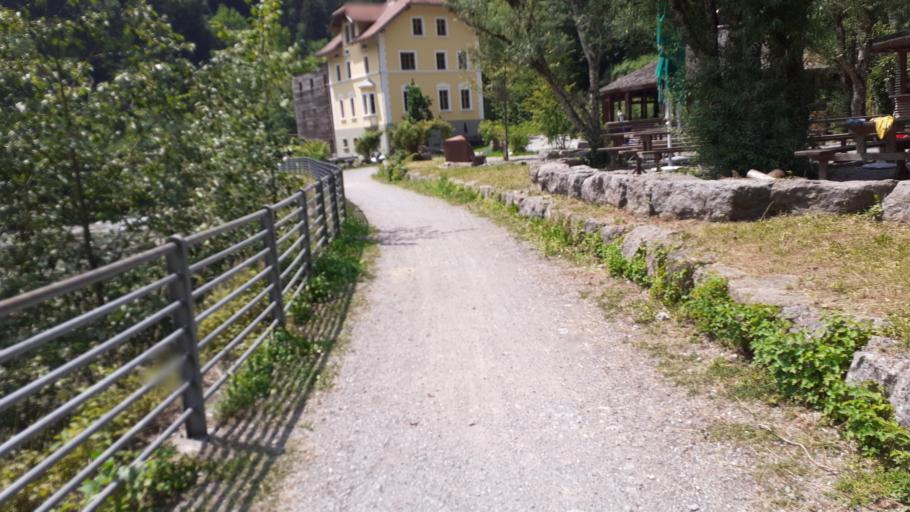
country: AT
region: Vorarlberg
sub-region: Politischer Bezirk Bregenz
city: Egg
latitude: 47.4467
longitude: 9.8906
